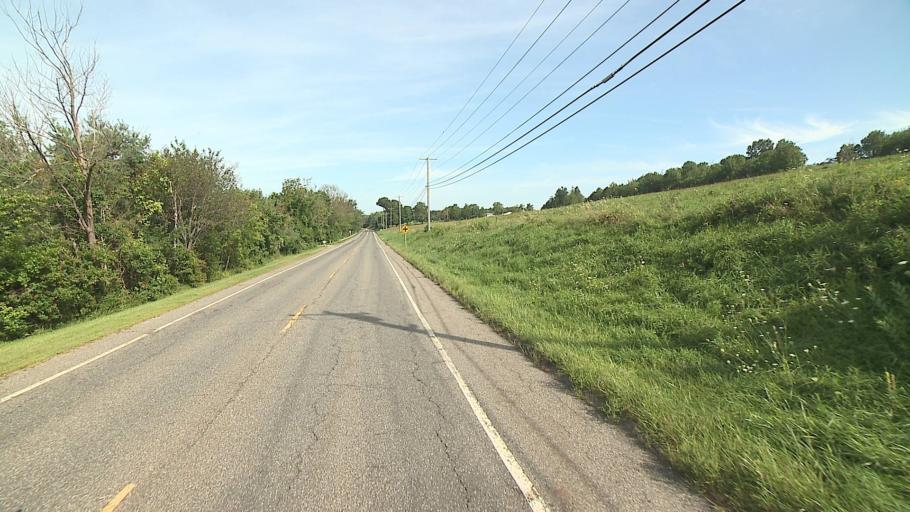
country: US
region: Connecticut
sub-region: Litchfield County
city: Litchfield
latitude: 41.7118
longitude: -73.1371
